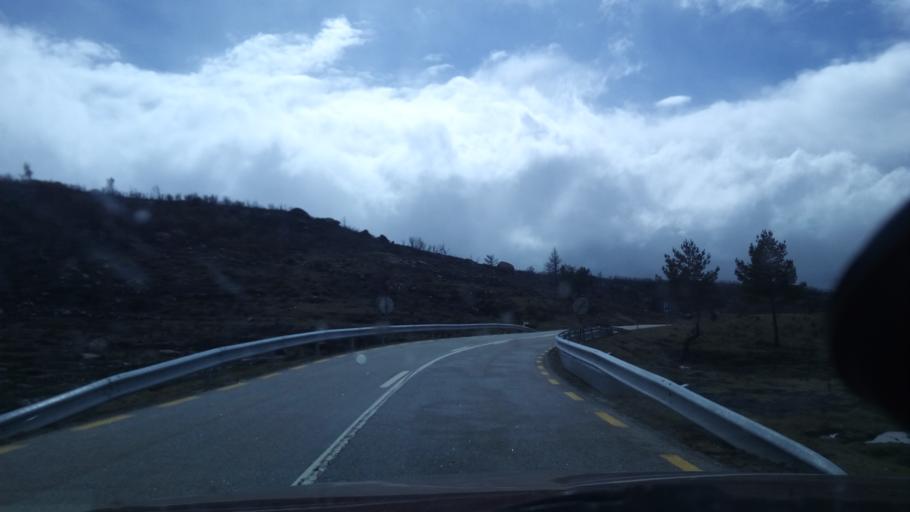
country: PT
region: Guarda
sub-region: Manteigas
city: Manteigas
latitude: 40.4192
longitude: -7.6012
